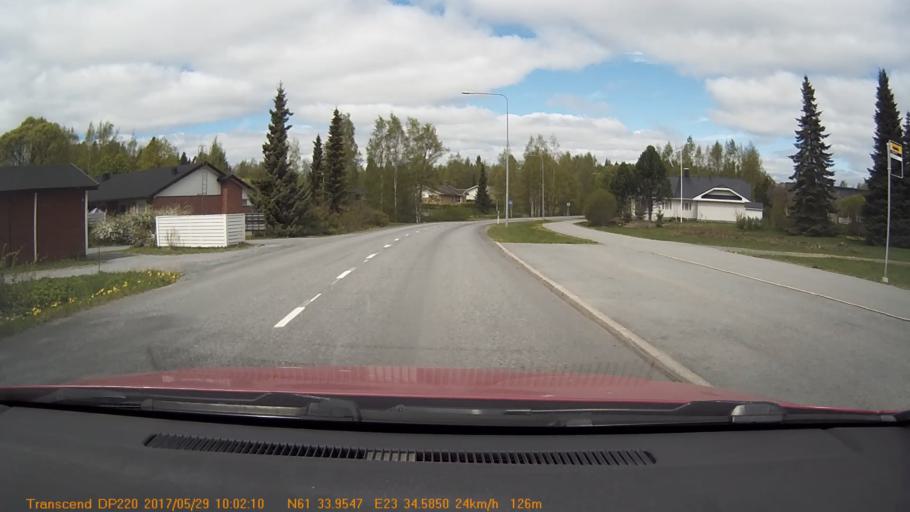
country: FI
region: Pirkanmaa
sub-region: Tampere
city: Yloejaervi
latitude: 61.5659
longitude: 23.5764
